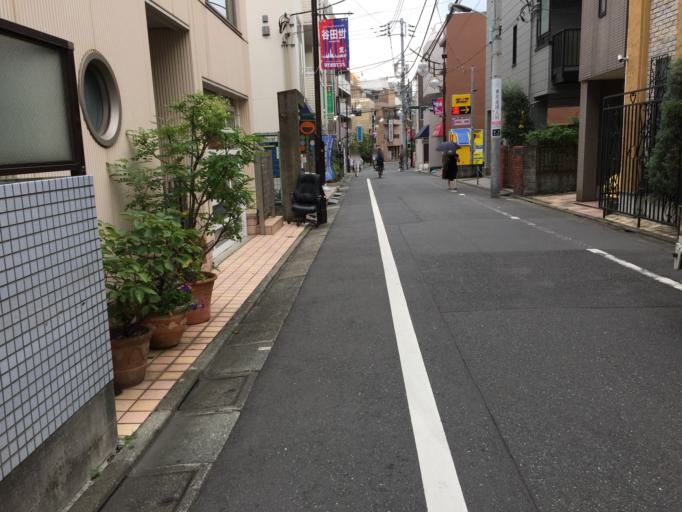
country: JP
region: Tokyo
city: Tokyo
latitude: 35.6644
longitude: 139.6415
